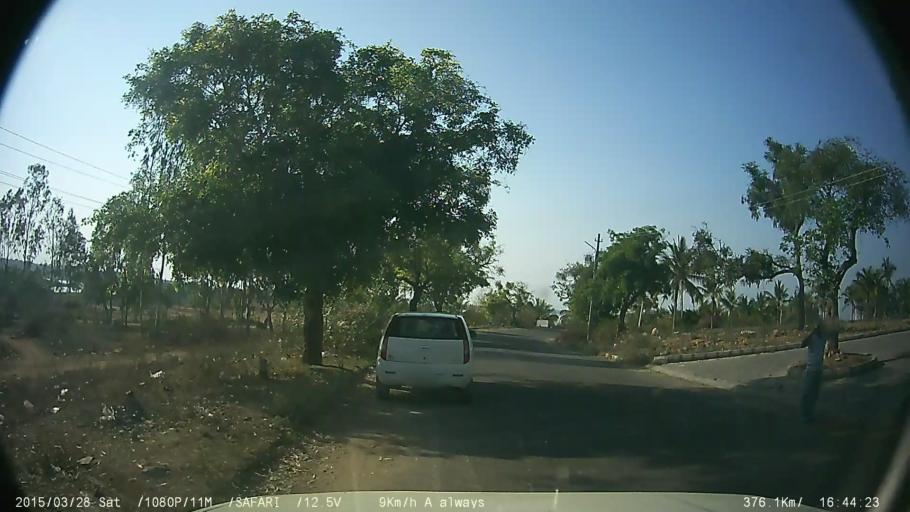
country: IN
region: Karnataka
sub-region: Mandya
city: Shrirangapattana
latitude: 12.4070
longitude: 76.5718
